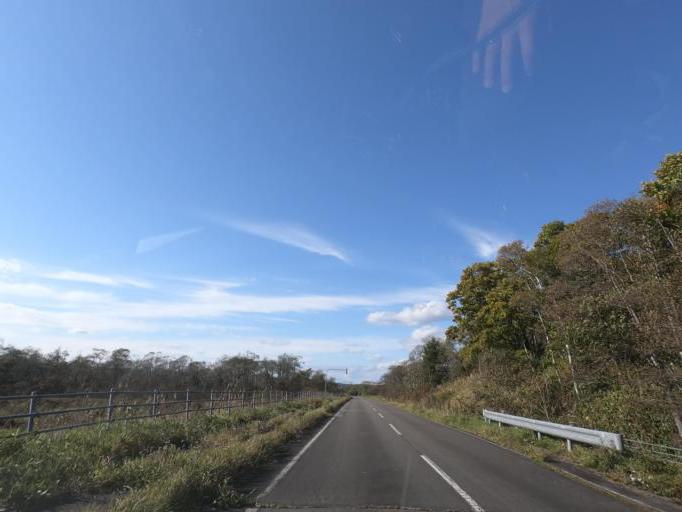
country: JP
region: Hokkaido
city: Obihiro
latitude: 42.6361
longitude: 143.5162
